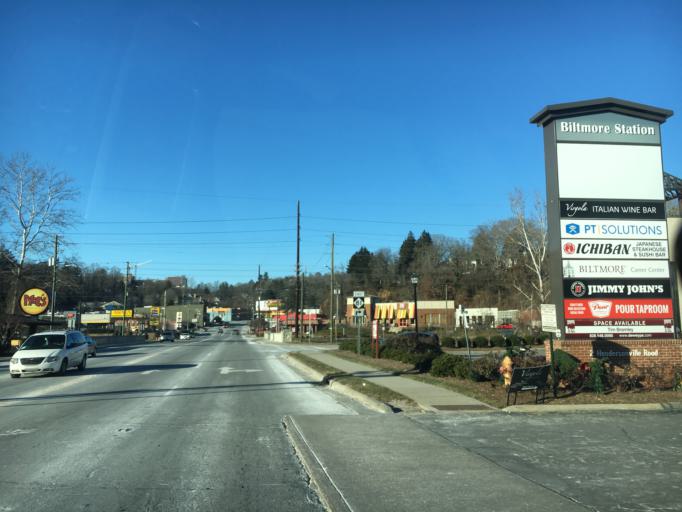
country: US
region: North Carolina
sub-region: Buncombe County
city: Asheville
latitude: 35.5680
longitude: -82.5440
